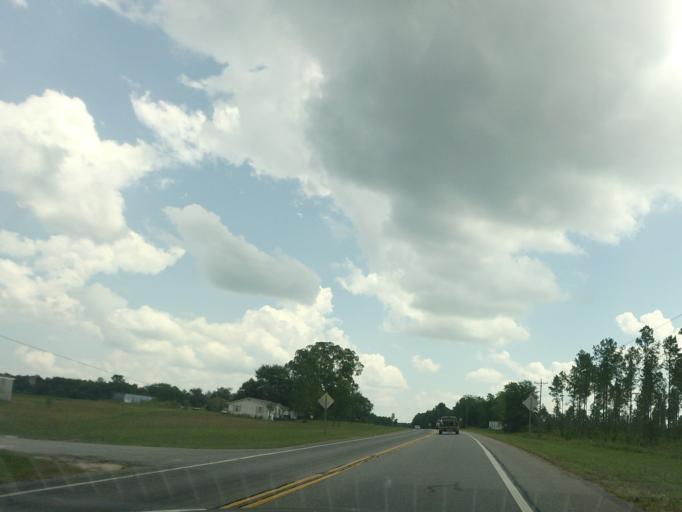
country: US
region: Georgia
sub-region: Bleckley County
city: Cochran
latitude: 32.4008
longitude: -83.3345
